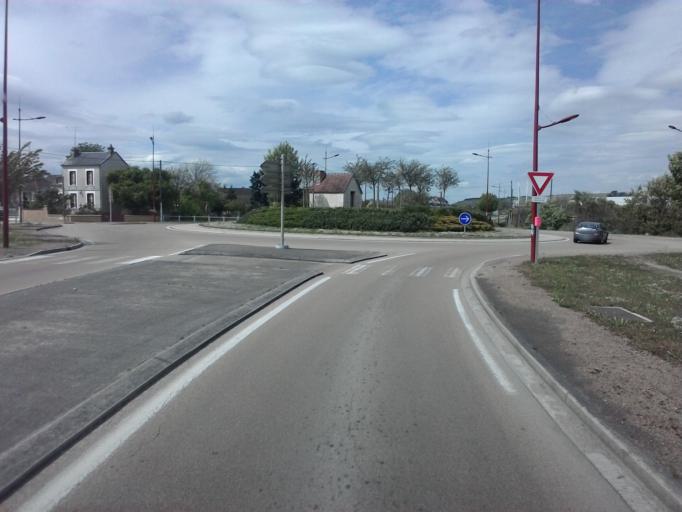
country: FR
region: Bourgogne
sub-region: Departement de l'Yonne
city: Champs-sur-Yonne
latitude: 47.7040
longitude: 3.6270
